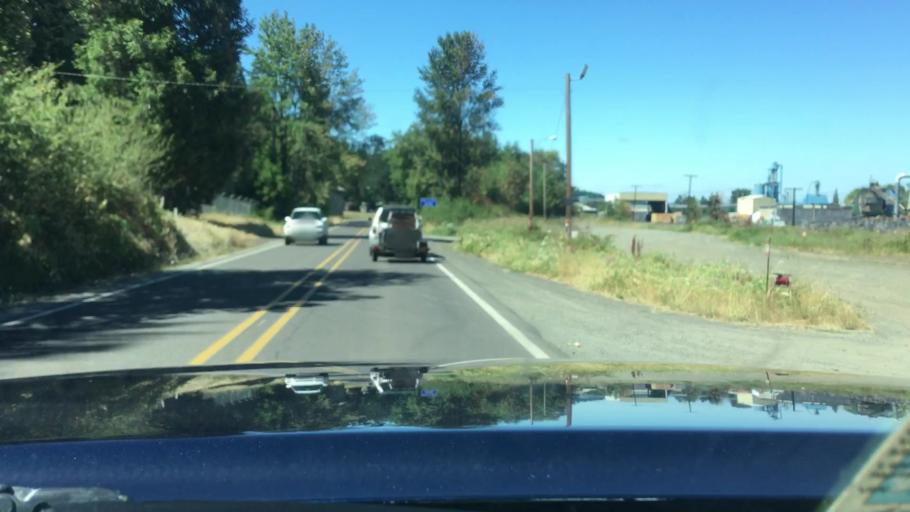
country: US
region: Oregon
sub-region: Lane County
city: Cottage Grove
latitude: 43.8287
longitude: -123.0447
